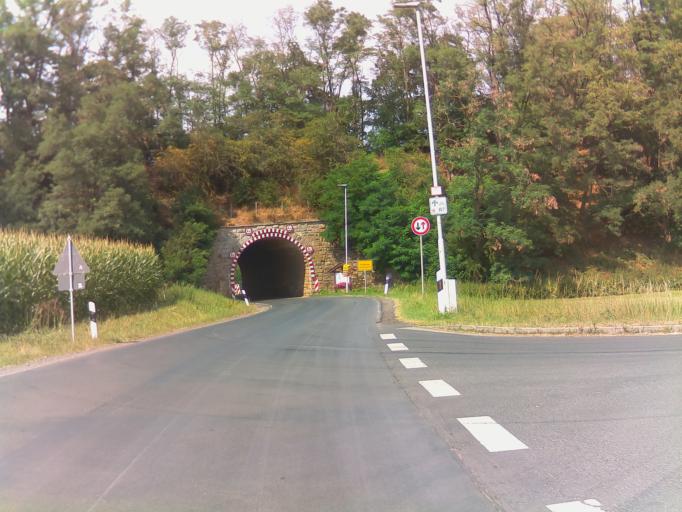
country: DE
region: Hesse
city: Grebenau
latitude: 50.7374
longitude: 9.4725
